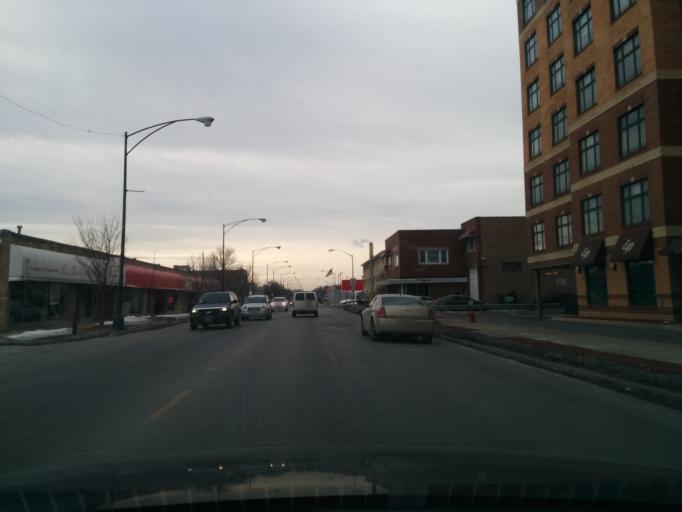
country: US
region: Illinois
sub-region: Cook County
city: Elmwood Park
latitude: 41.9157
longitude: -87.8061
